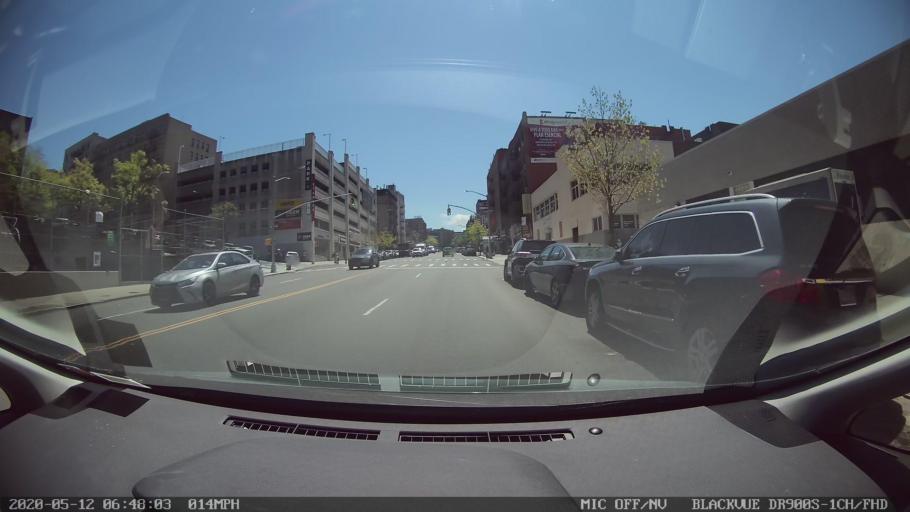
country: US
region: New York
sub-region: New York County
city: Inwood
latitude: 40.8531
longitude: -73.9343
